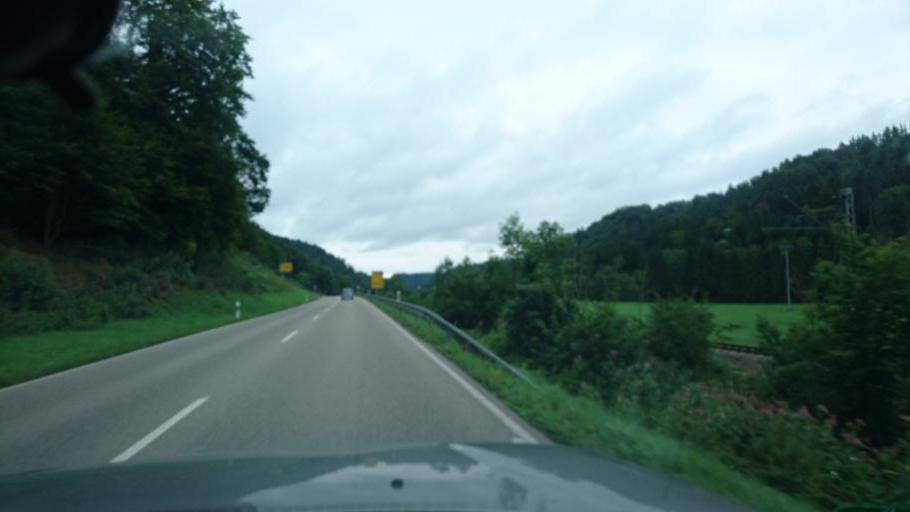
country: DE
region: Baden-Wuerttemberg
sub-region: Freiburg Region
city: Sulz am Neckar
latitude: 48.3552
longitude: 8.6032
